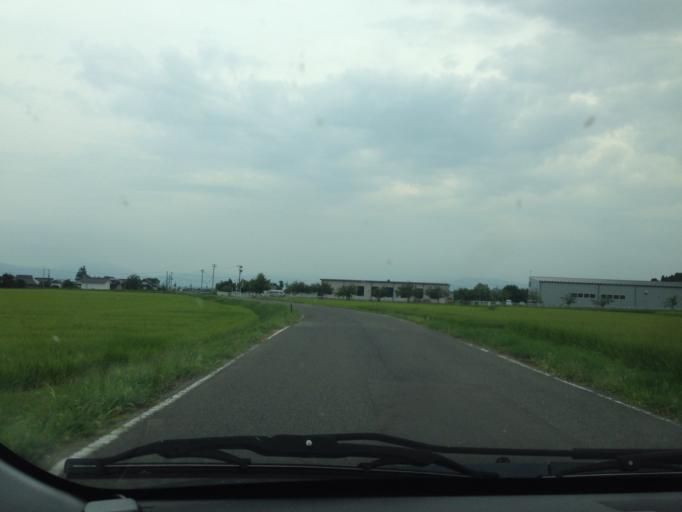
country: JP
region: Fukushima
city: Kitakata
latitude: 37.6498
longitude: 139.8453
